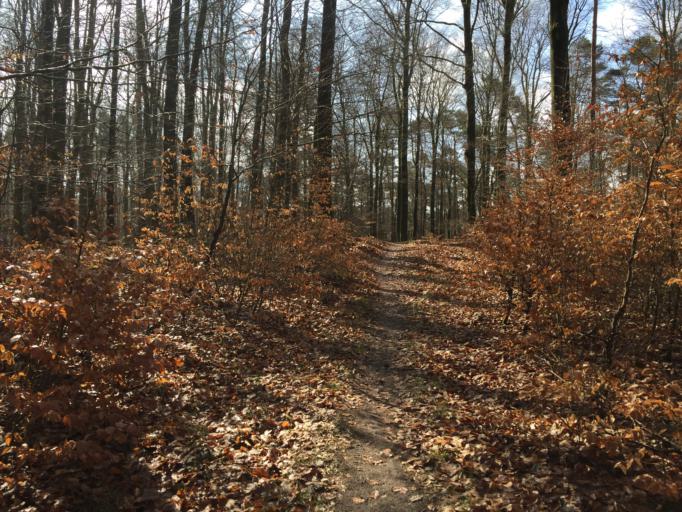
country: DE
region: Rheinland-Pfalz
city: Frankenstein
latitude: 49.4146
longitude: 7.9500
